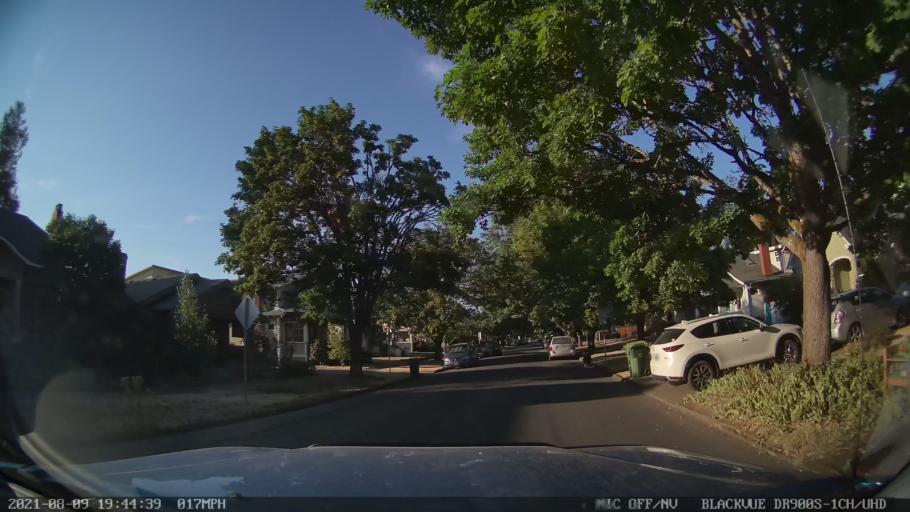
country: US
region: Oregon
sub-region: Marion County
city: Salem
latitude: 44.9482
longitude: -123.0315
